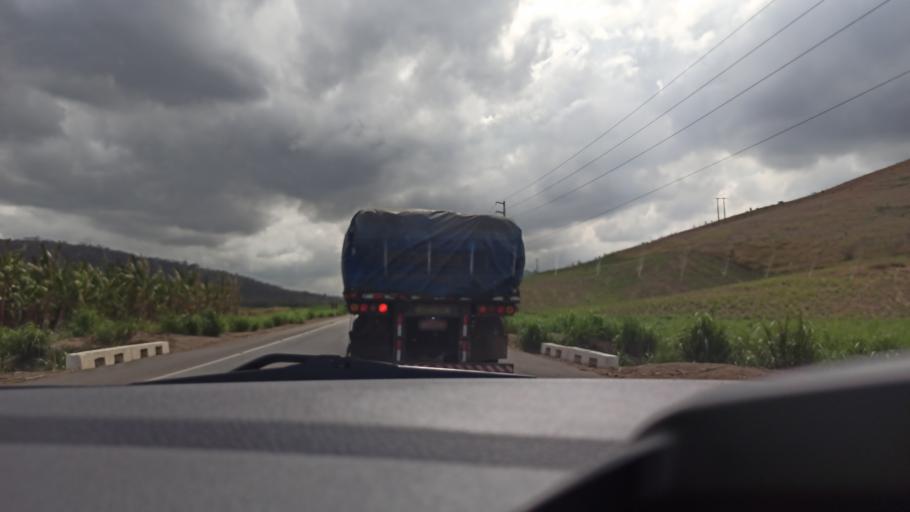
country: BR
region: Pernambuco
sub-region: Timbauba
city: Timbauba
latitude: -7.5225
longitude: -35.2984
